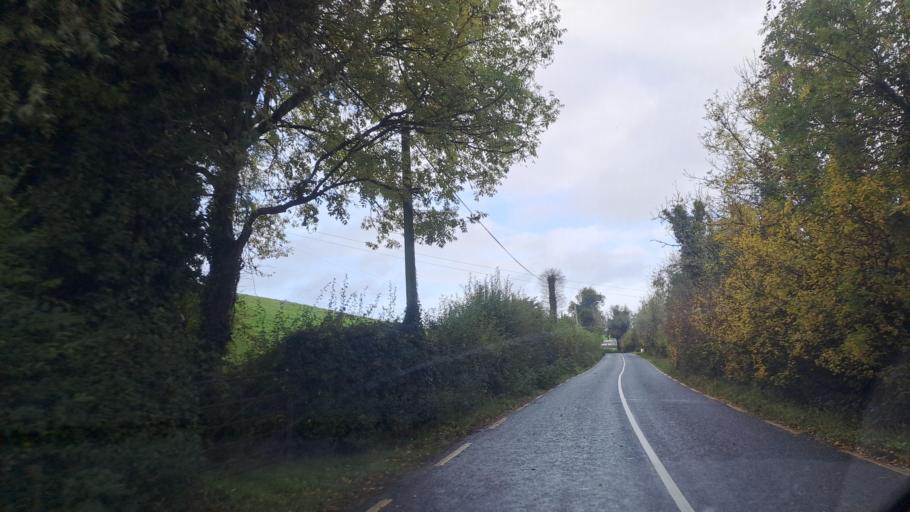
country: IE
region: Ulster
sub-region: County Monaghan
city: Carrickmacross
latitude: 53.9136
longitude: -6.7081
